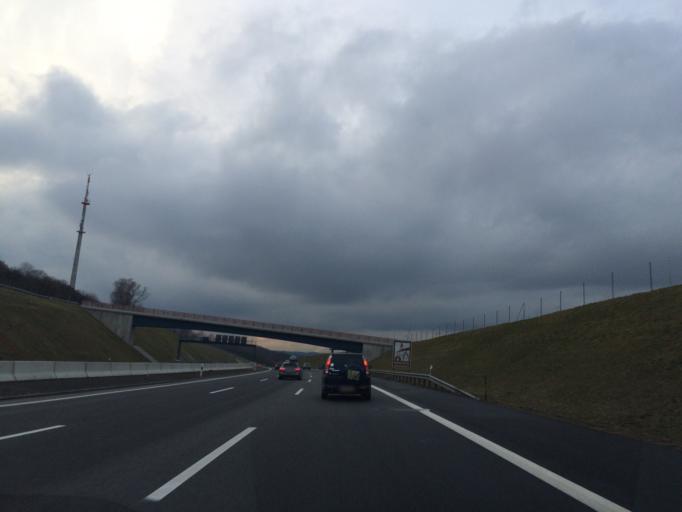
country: DE
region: Bavaria
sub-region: Regierungsbezirk Unterfranken
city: Waldaschaff
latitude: 49.9709
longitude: 9.2938
